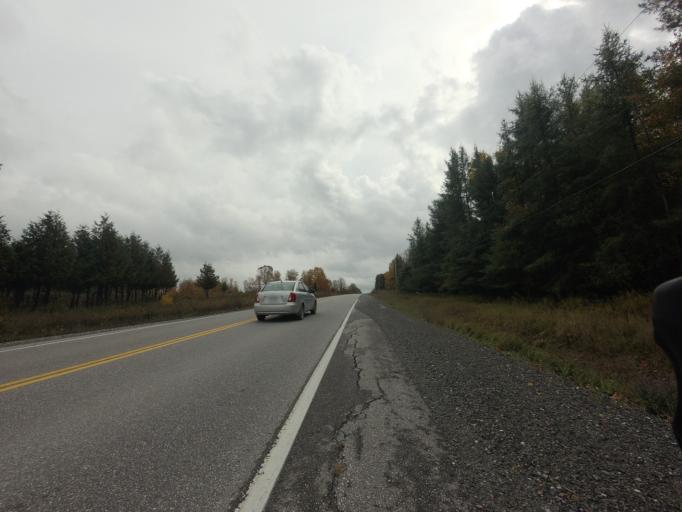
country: CA
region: Ontario
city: Perth
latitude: 45.1005
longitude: -76.4691
